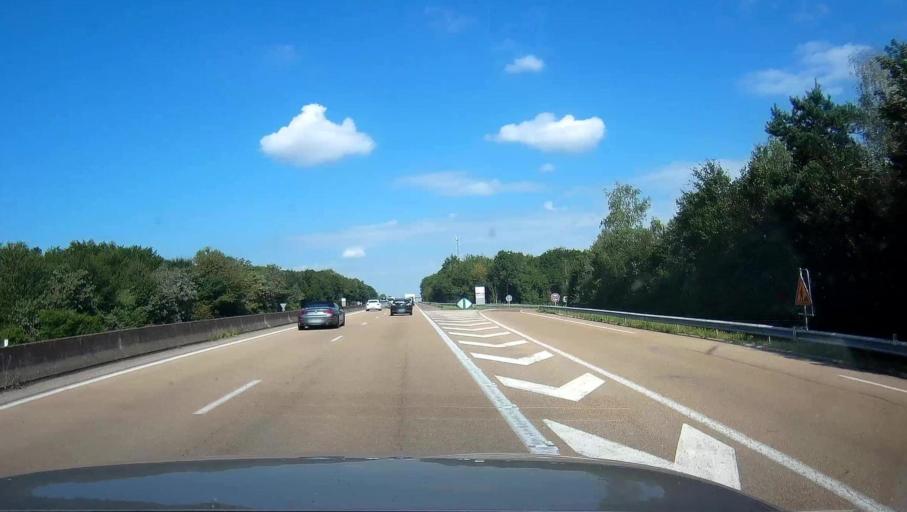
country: FR
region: Champagne-Ardenne
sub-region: Departement de la Haute-Marne
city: Chamarandes-Choignes
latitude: 47.9610
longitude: 5.1520
